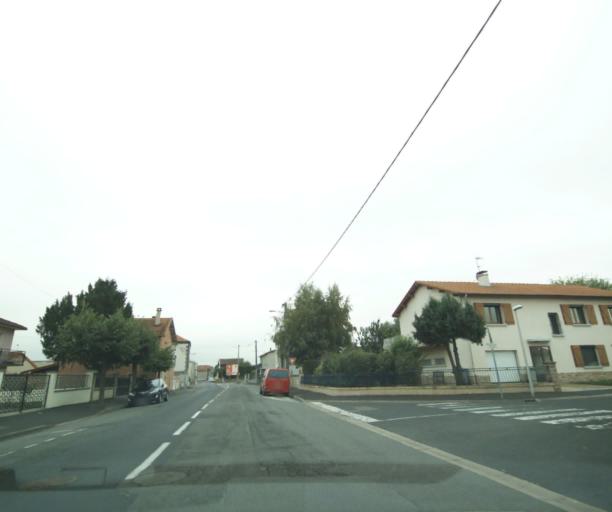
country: FR
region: Auvergne
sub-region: Departement du Puy-de-Dome
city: Gerzat
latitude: 45.8294
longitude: 3.1456
